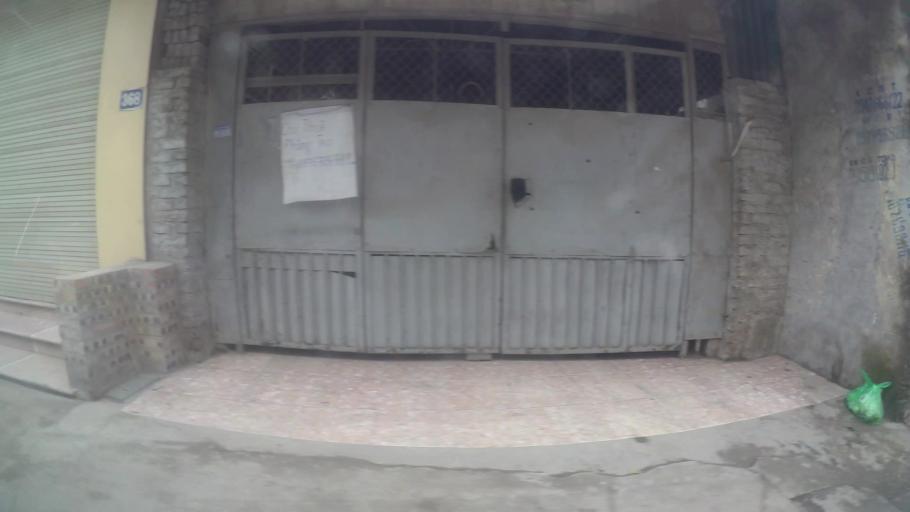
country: VN
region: Ha Noi
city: Tay Ho
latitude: 21.0716
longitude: 105.7902
